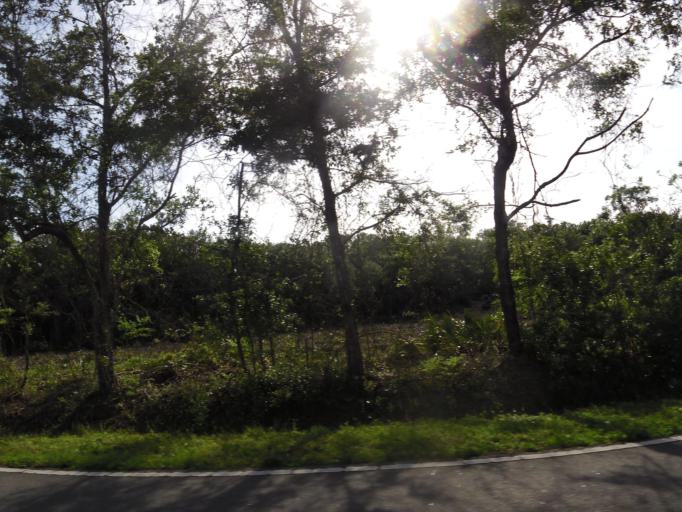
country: US
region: Florida
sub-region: Duval County
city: Atlantic Beach
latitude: 30.4939
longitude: -81.4720
